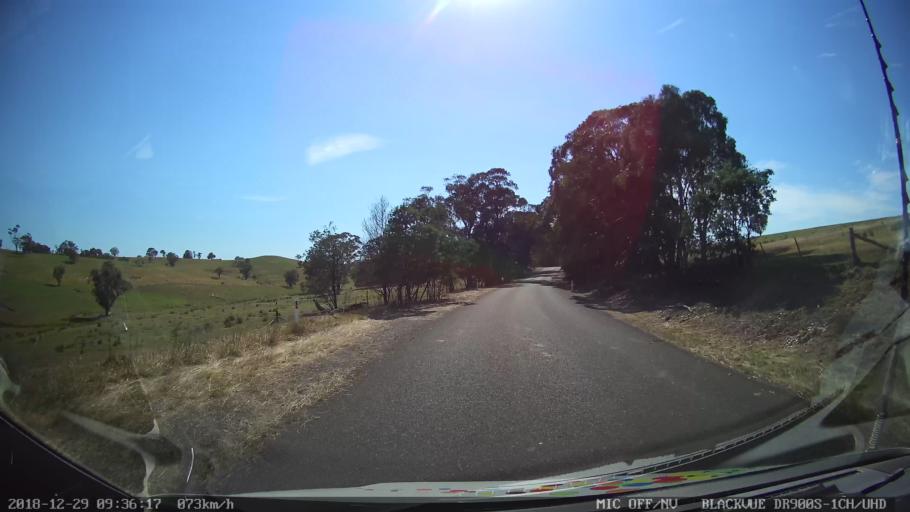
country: AU
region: New South Wales
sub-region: Upper Lachlan Shire
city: Crookwell
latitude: -34.6334
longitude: 149.3620
